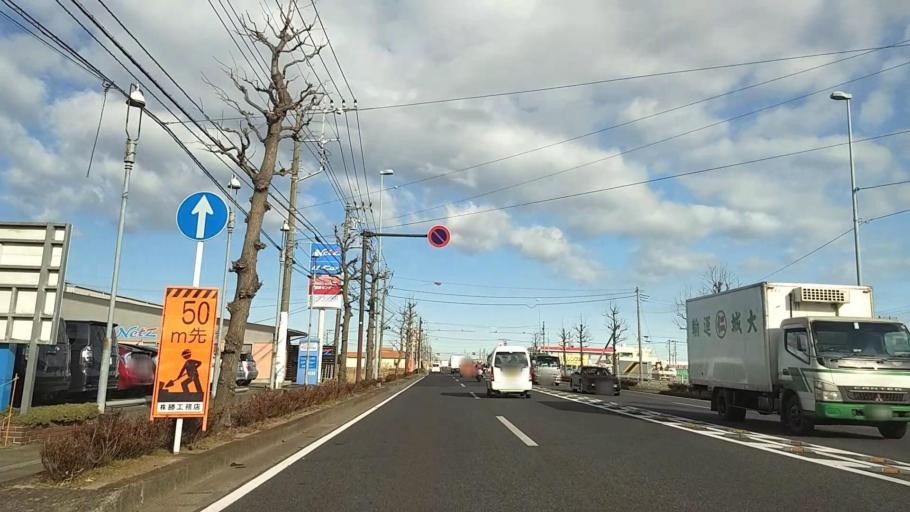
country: JP
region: Kanagawa
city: Atsugi
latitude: 35.3865
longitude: 139.3616
